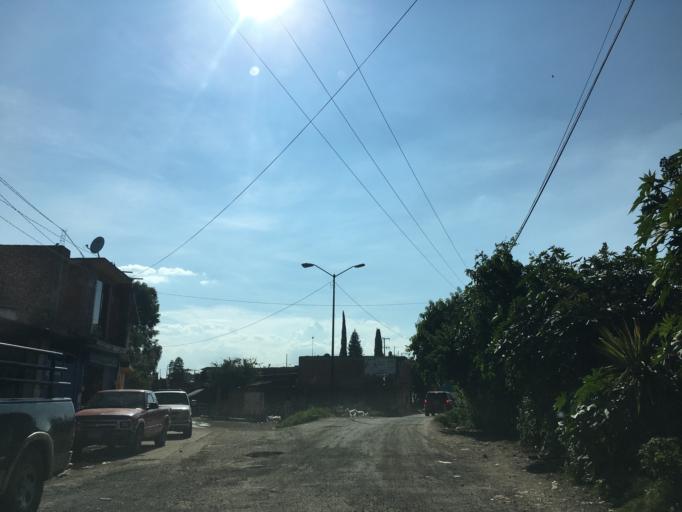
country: MX
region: Michoacan
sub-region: Morelia
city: La Mintzita (Piedra Dura)
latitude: 19.5948
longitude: -101.2818
